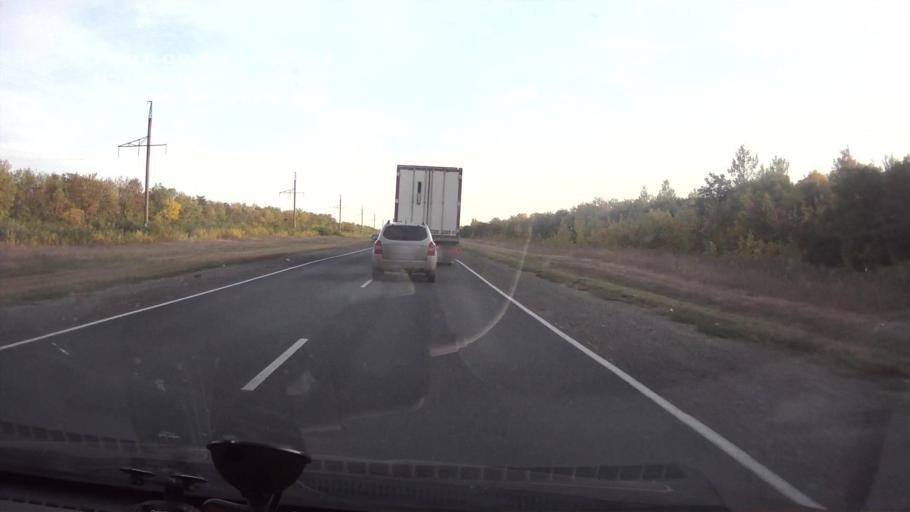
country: RU
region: Saratov
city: Krasnoarmeysk
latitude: 51.1323
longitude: 45.6503
